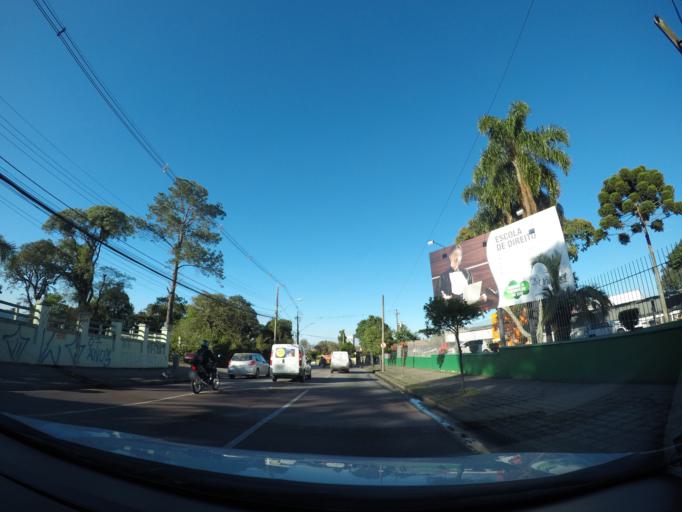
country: BR
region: Parana
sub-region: Curitiba
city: Curitiba
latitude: -25.4071
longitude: -49.2762
